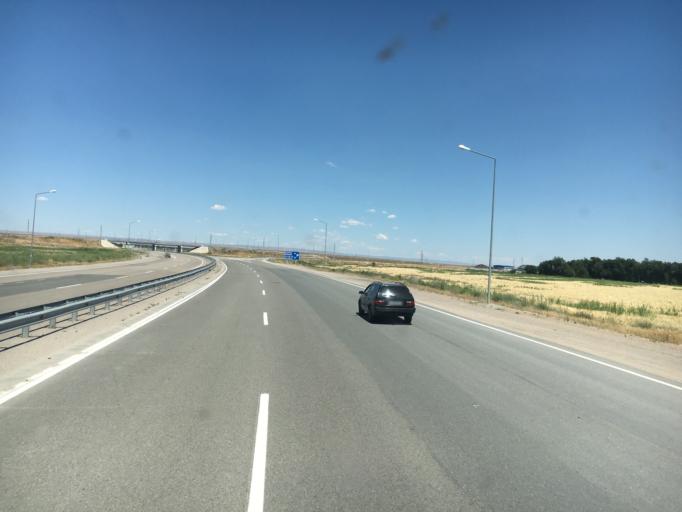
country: KG
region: Chuy
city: Sokuluk
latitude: 43.2707
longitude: 74.2261
